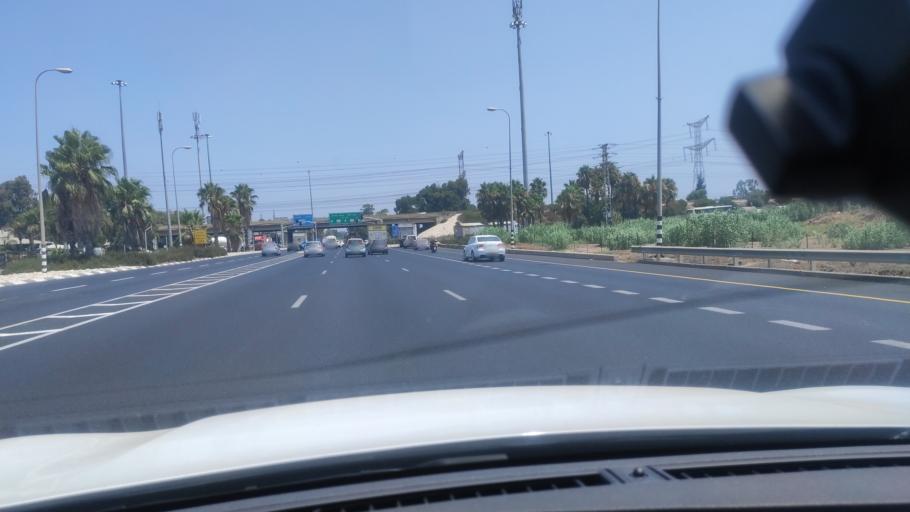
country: IL
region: Central District
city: Petah Tiqwa
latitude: 32.1194
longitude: 34.9035
